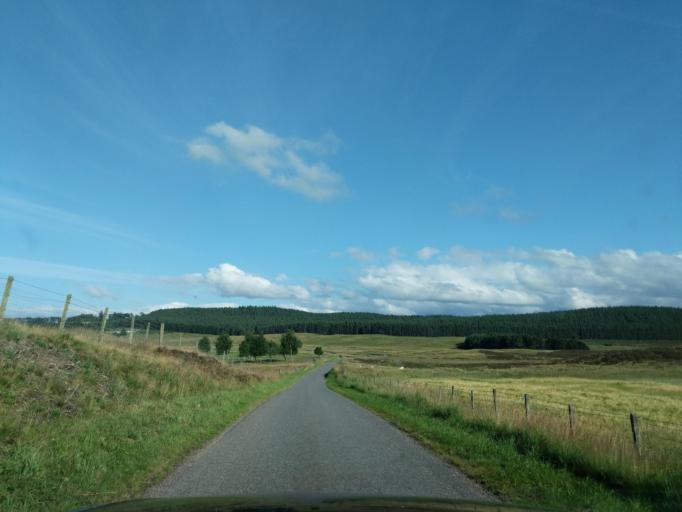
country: GB
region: Scotland
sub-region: Highland
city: Grantown on Spey
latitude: 57.2910
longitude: -3.7374
